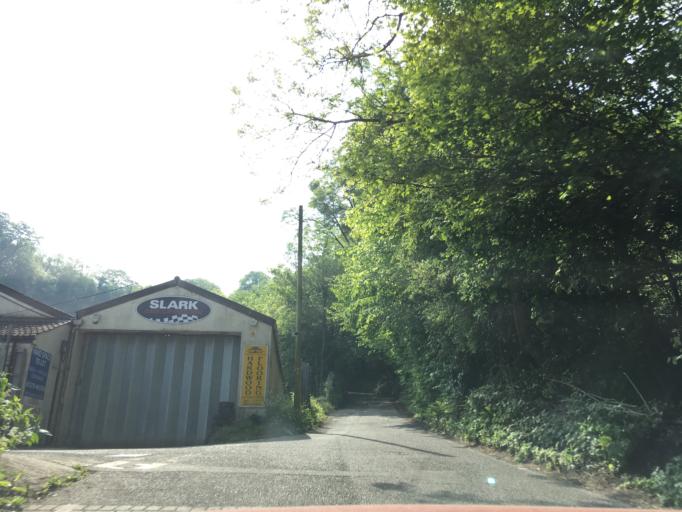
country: GB
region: England
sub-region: North Somerset
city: Nailsea
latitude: 51.4094
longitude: -2.7300
